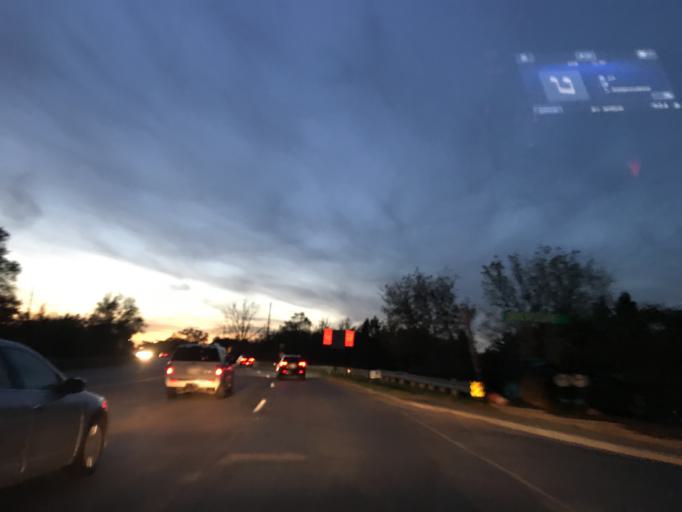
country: US
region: Michigan
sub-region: Wayne County
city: Northville
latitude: 42.4398
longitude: -83.4713
